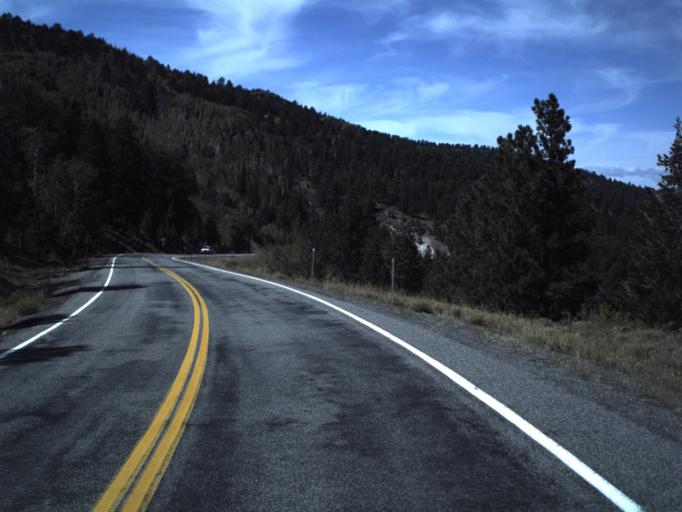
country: US
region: Utah
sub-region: Wayne County
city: Loa
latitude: 38.1474
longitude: -111.3274
